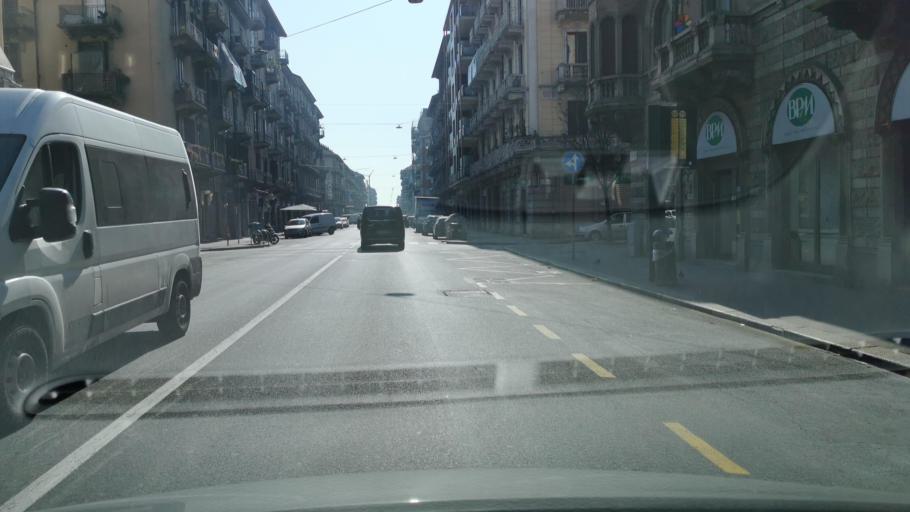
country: IT
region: Piedmont
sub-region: Provincia di Torino
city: Turin
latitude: 45.0949
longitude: 7.6913
